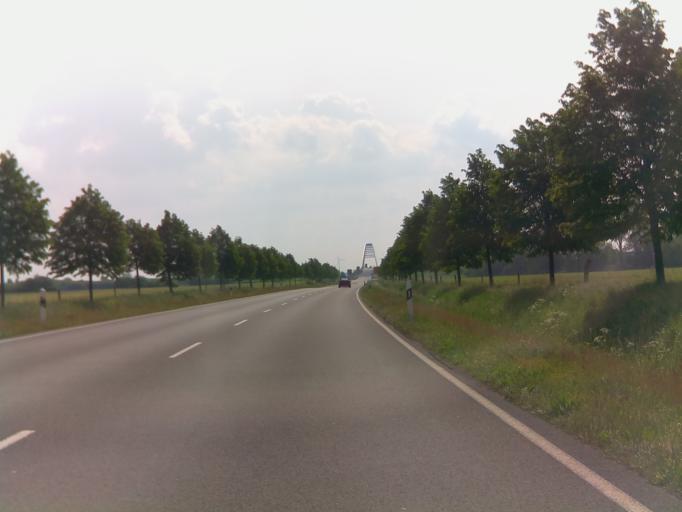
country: DE
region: Saxony-Anhalt
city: Tangermunde
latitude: 52.5707
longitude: 11.9674
